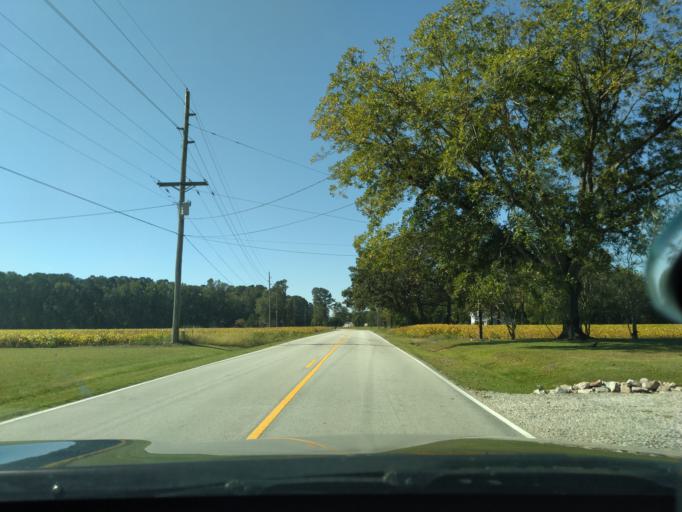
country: US
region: North Carolina
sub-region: Beaufort County
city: River Road
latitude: 35.5724
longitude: -76.9723
